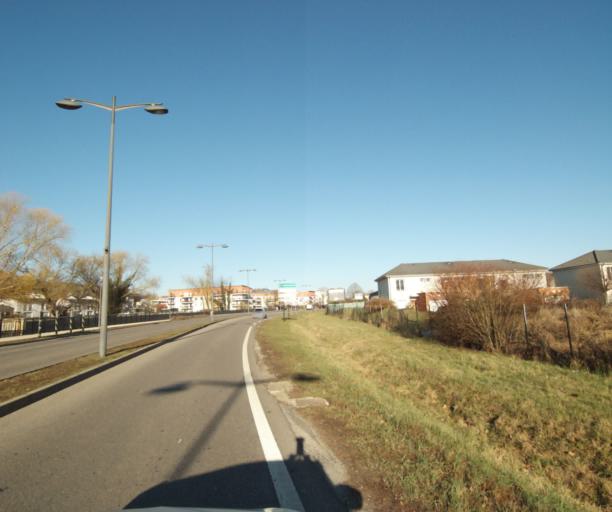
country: FR
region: Lorraine
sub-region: Departement de Meurthe-et-Moselle
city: Essey-les-Nancy
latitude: 48.7022
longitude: 6.2264
